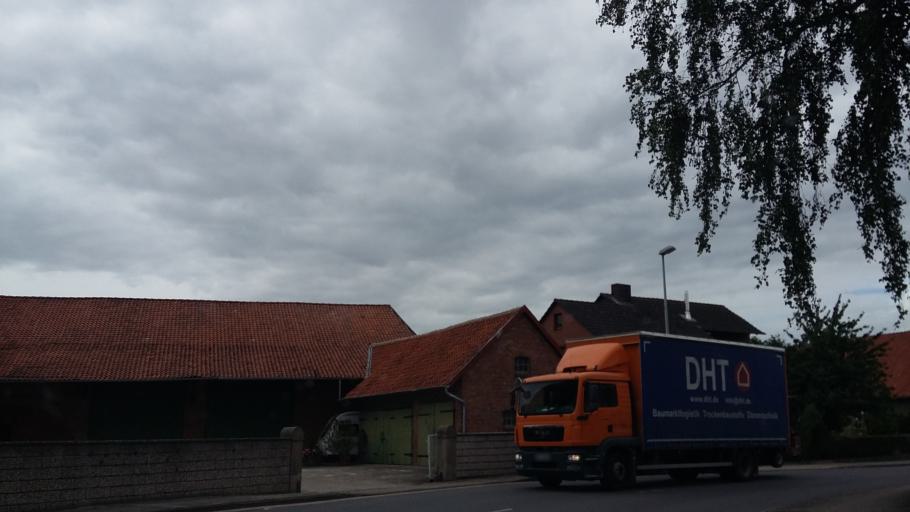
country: DE
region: Lower Saxony
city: Giesen
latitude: 52.2140
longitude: 9.9268
